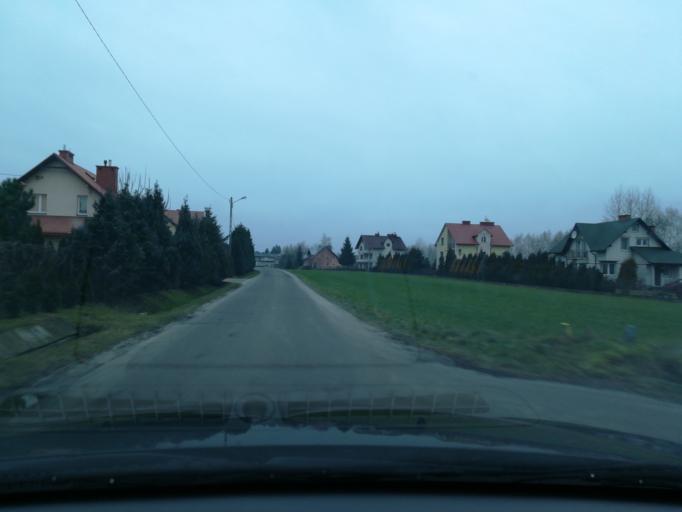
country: PL
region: Subcarpathian Voivodeship
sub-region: Powiat lancucki
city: Kosina
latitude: 50.0820
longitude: 22.3315
